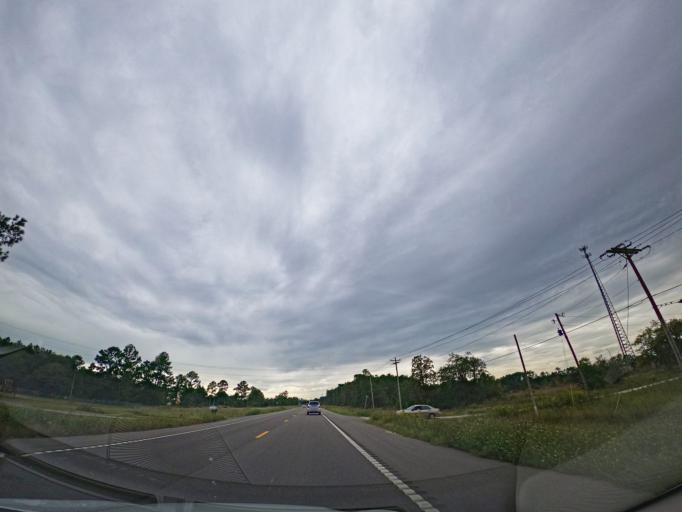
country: US
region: Mississippi
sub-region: Hancock County
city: Pearlington
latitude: 30.2454
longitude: -89.6003
